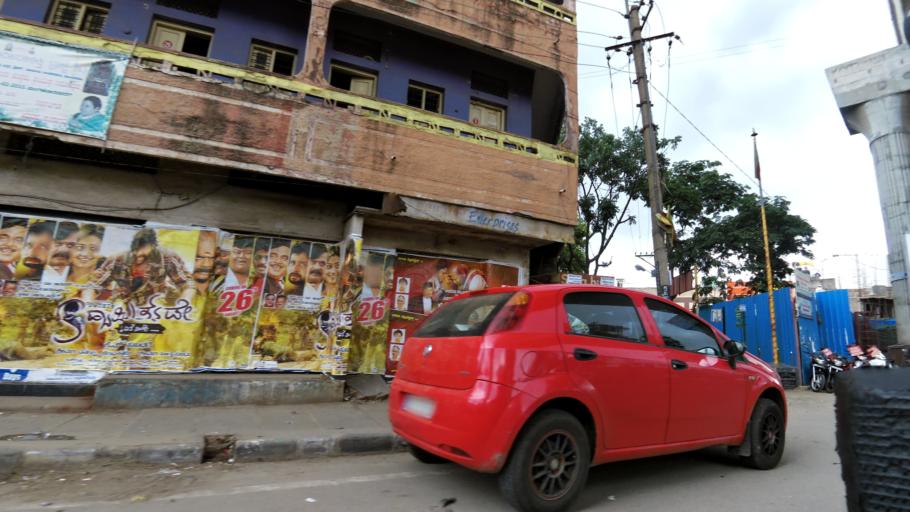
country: IN
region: Karnataka
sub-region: Bangalore Urban
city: Bangalore
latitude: 12.9777
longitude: 77.6271
